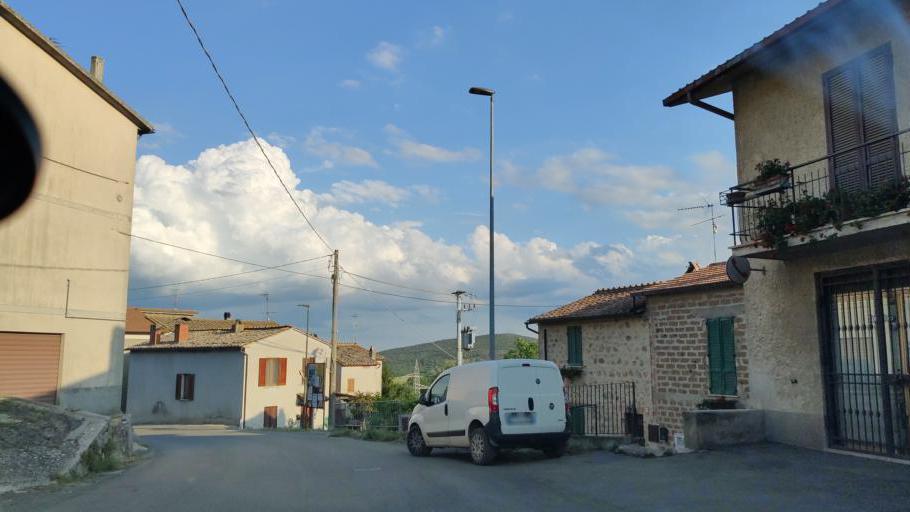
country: IT
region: Umbria
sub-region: Provincia di Terni
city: Lugnano in Teverina
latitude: 42.5957
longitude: 12.3680
